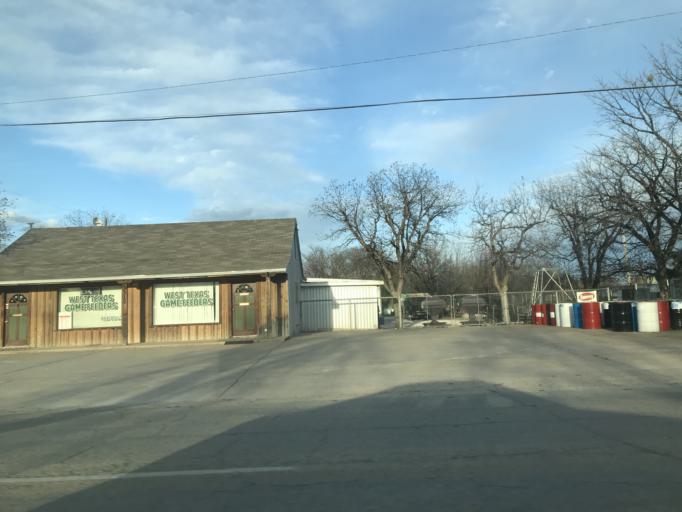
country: US
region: Texas
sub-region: Tom Green County
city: San Angelo
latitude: 31.4954
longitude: -100.4580
